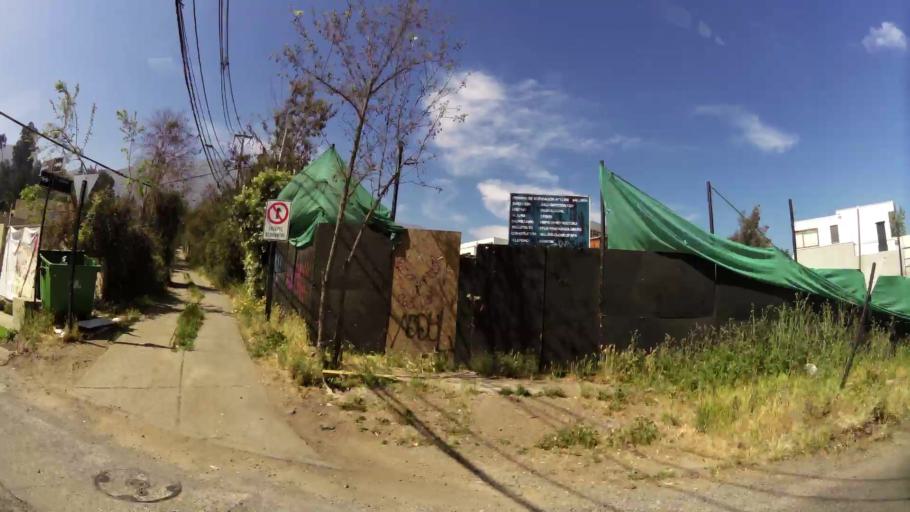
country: CL
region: Santiago Metropolitan
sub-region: Provincia de Santiago
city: Villa Presidente Frei, Nunoa, Santiago, Chile
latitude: -33.4433
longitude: -70.5226
